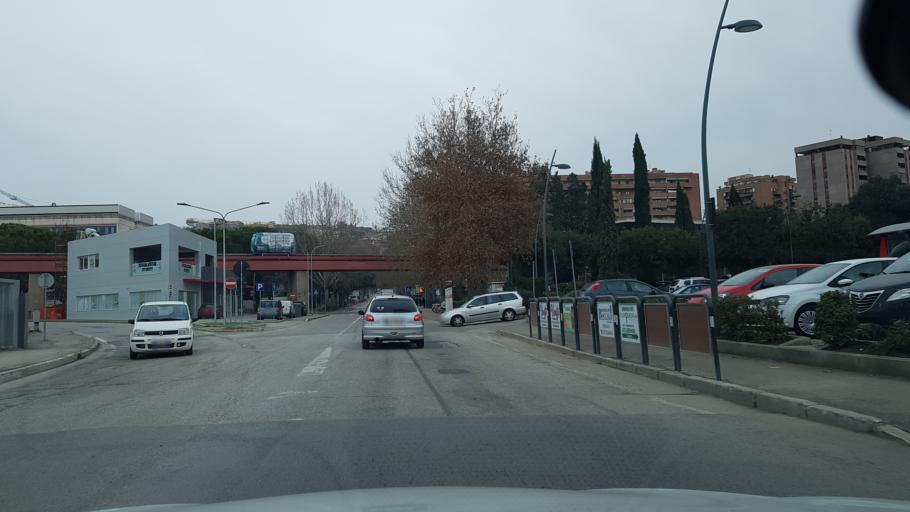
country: IT
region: Umbria
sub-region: Provincia di Perugia
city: Perugia
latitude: 43.1062
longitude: 12.3623
